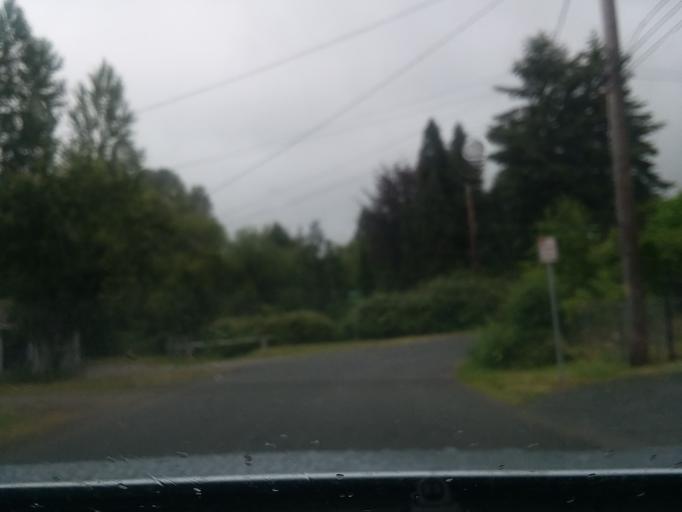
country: US
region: Washington
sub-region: King County
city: Shoreline
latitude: 47.7378
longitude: -122.3323
